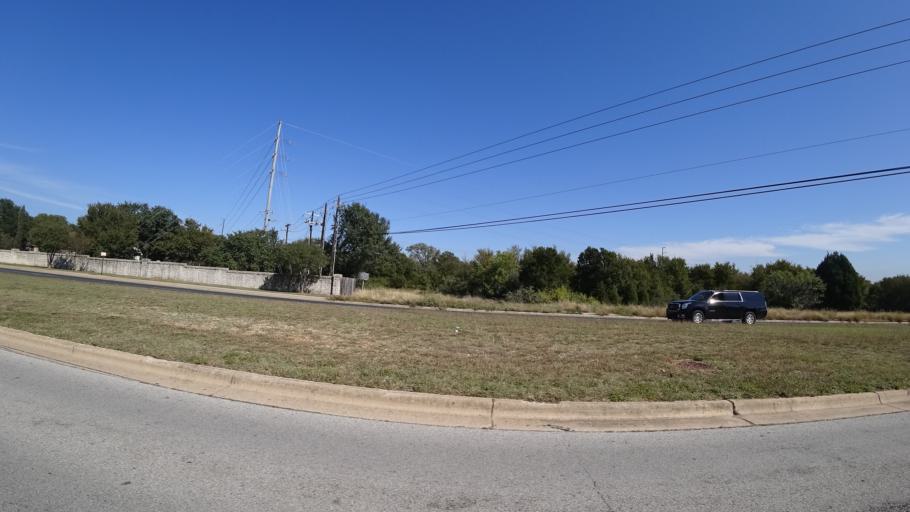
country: US
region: Texas
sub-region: Travis County
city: Shady Hollow
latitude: 30.1925
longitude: -97.8584
